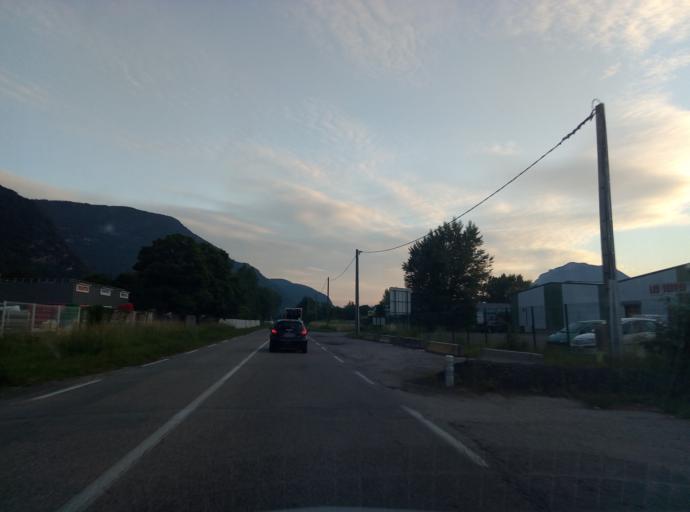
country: FR
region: Rhone-Alpes
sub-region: Departement de l'Isere
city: Noyarey
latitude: 45.2563
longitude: 5.6280
